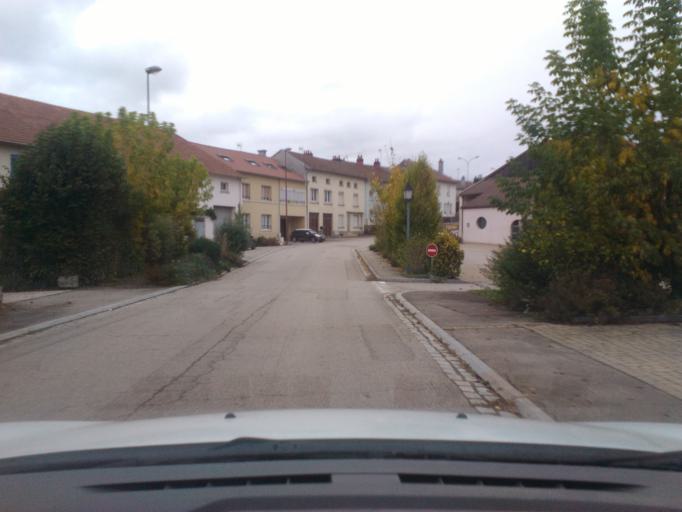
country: FR
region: Lorraine
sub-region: Departement des Vosges
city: Deyvillers
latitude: 48.2001
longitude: 6.4879
